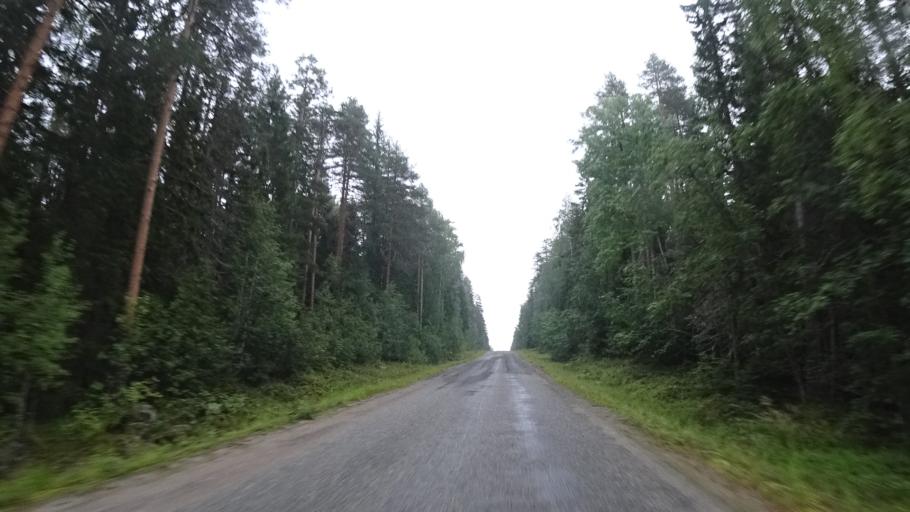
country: FI
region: North Karelia
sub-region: Joensuu
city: Ilomantsi
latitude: 63.2277
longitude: 30.8449
